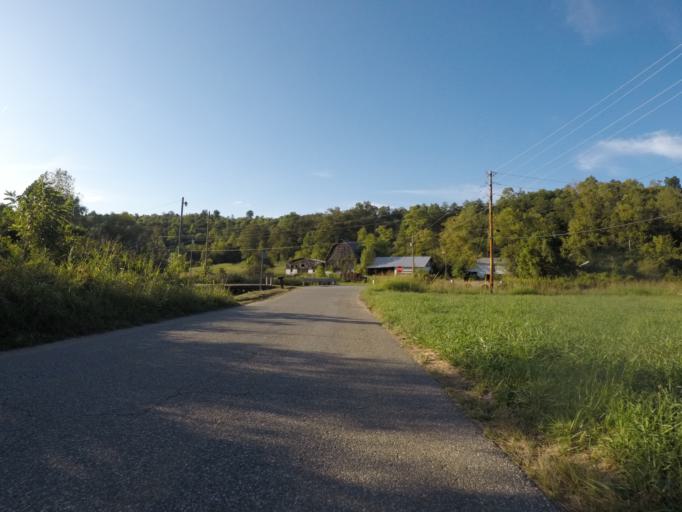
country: US
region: Ohio
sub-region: Lawrence County
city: Coal Grove
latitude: 38.5377
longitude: -82.5334
